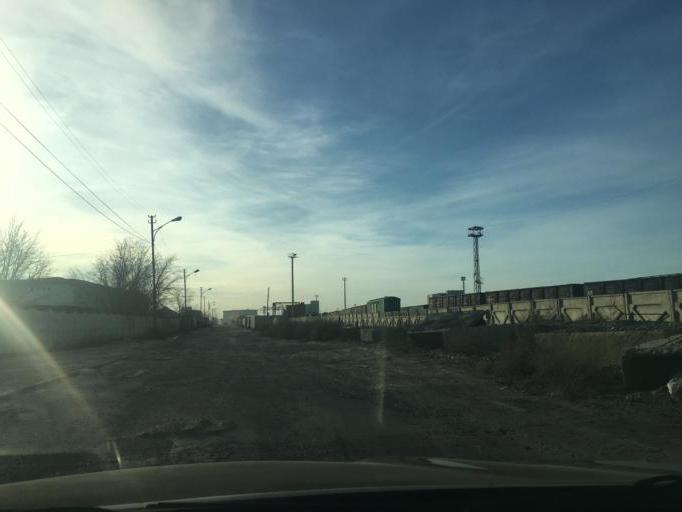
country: MN
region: Ulaanbaatar
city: Ulaanbaatar
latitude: 47.9072
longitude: 106.8901
